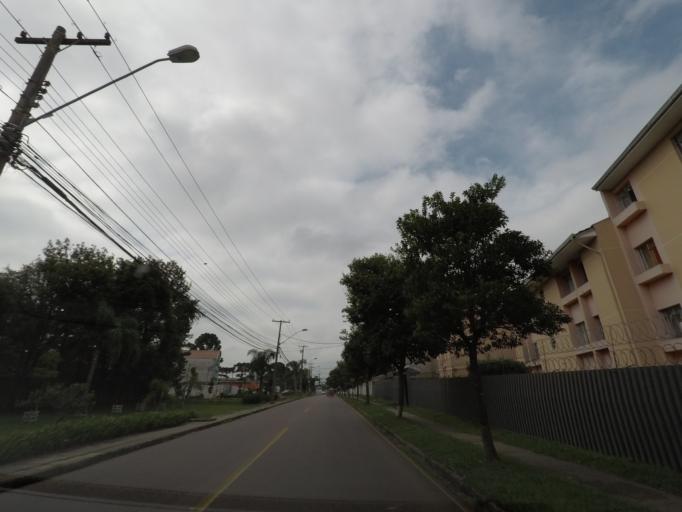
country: BR
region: Parana
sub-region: Curitiba
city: Curitiba
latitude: -25.4955
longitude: -49.3213
